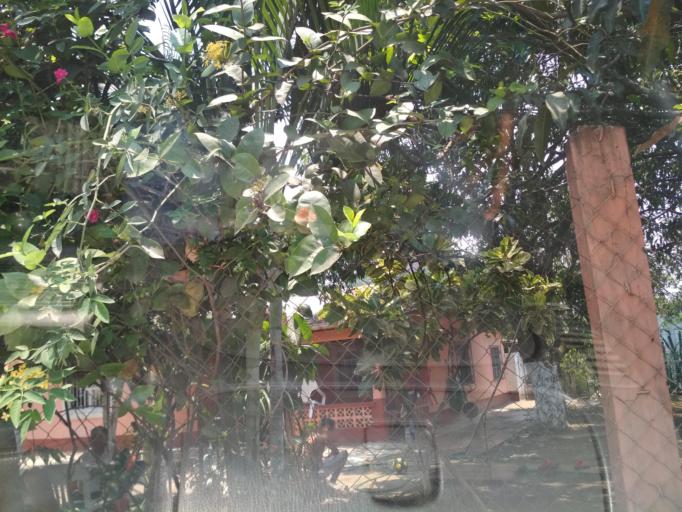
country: MX
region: Veracruz
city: Cosolapa
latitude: 18.5907
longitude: -96.6963
